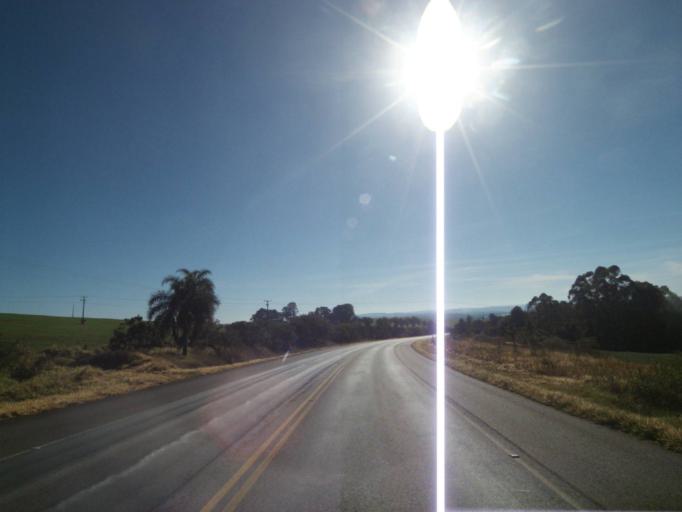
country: BR
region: Parana
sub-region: Tibagi
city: Tibagi
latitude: -24.4954
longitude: -50.4447
